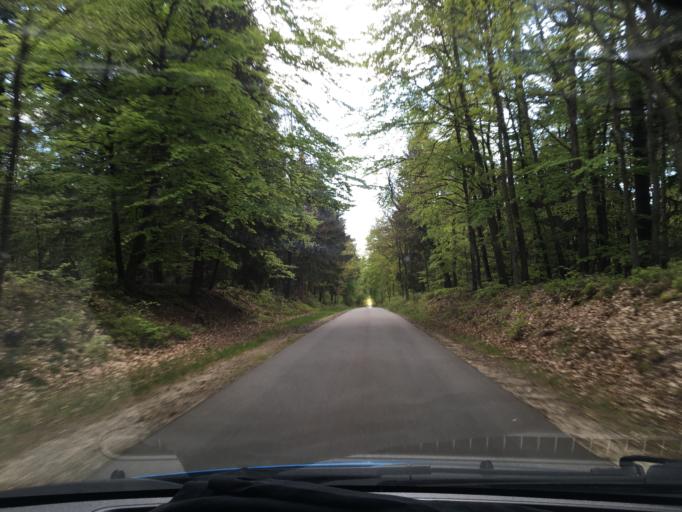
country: DE
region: Lower Saxony
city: Nahrendorf
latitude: 53.1352
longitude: 10.8004
